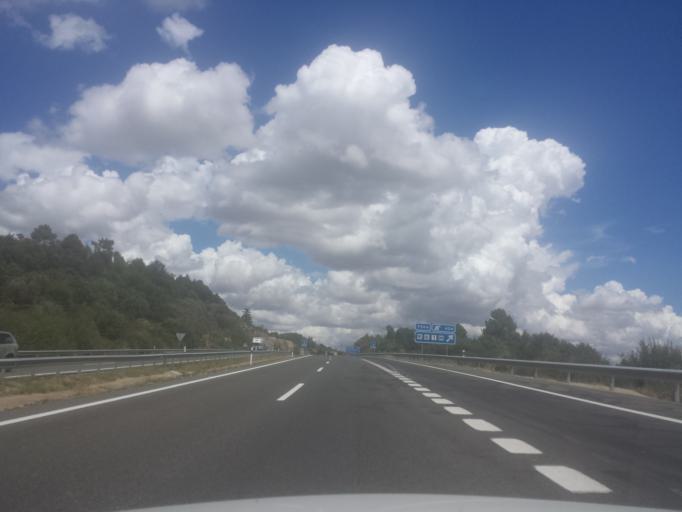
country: ES
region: Castille and Leon
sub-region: Provincia de Salamanca
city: Penacaballera
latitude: 40.3376
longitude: -5.8514
